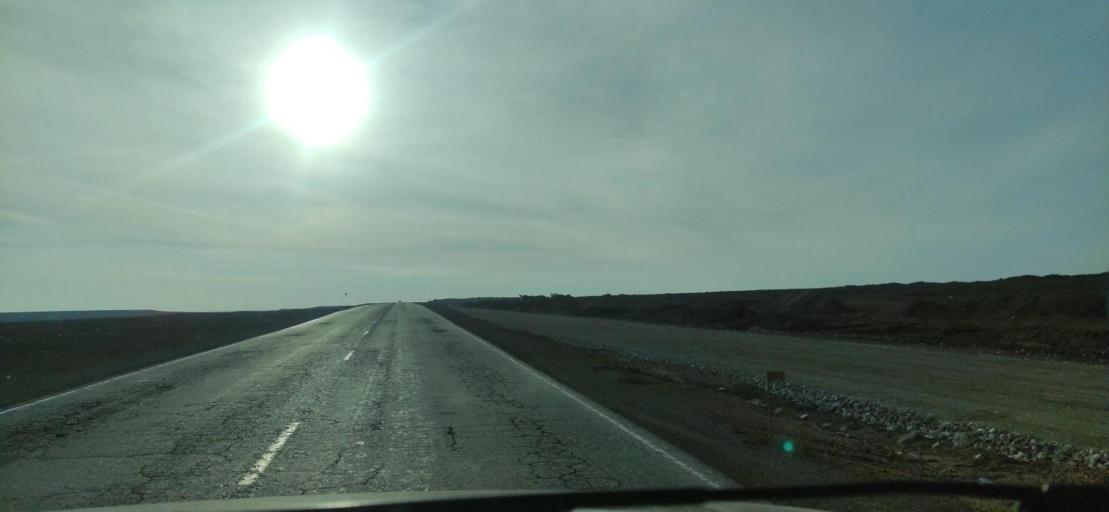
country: KZ
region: Qaraghandy
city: Saryshaghan
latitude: 46.3320
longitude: 73.8002
